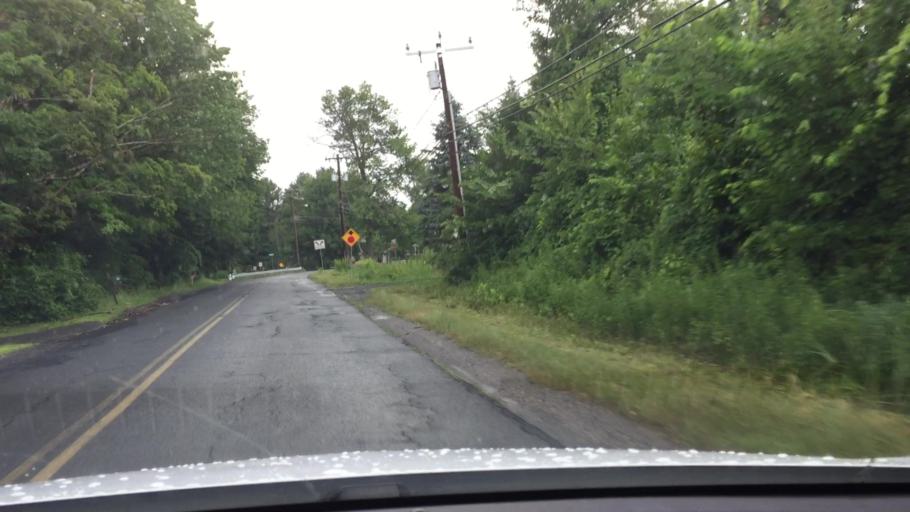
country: US
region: Massachusetts
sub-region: Berkshire County
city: Pittsfield
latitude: 42.4291
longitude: -73.1960
